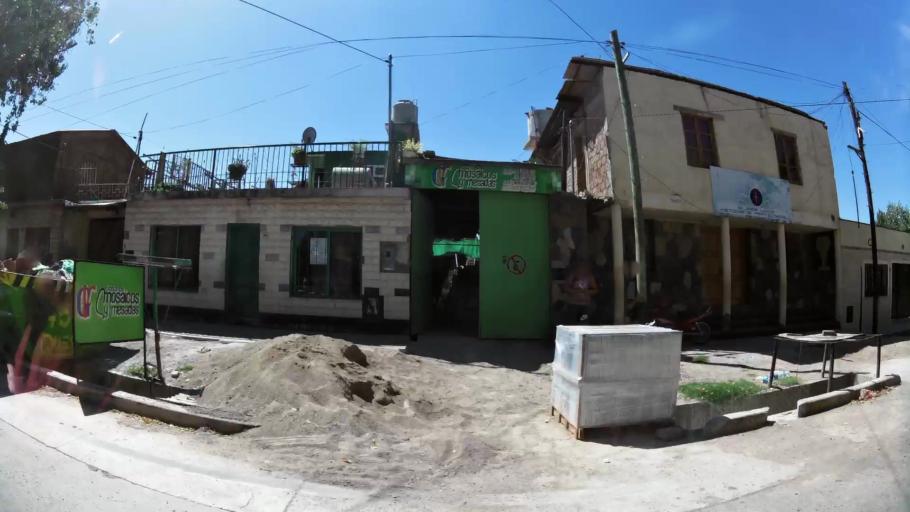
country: AR
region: Mendoza
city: Mendoza
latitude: -32.8760
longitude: -68.8201
